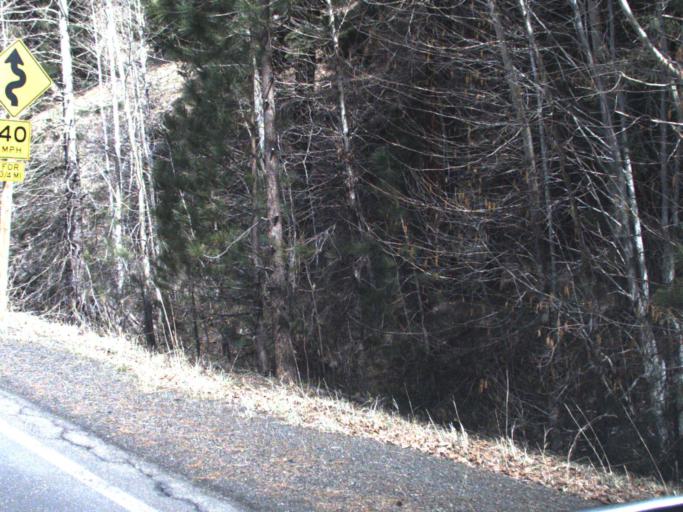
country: US
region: Washington
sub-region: Kittitas County
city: Cle Elum
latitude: 46.9879
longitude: -121.0931
